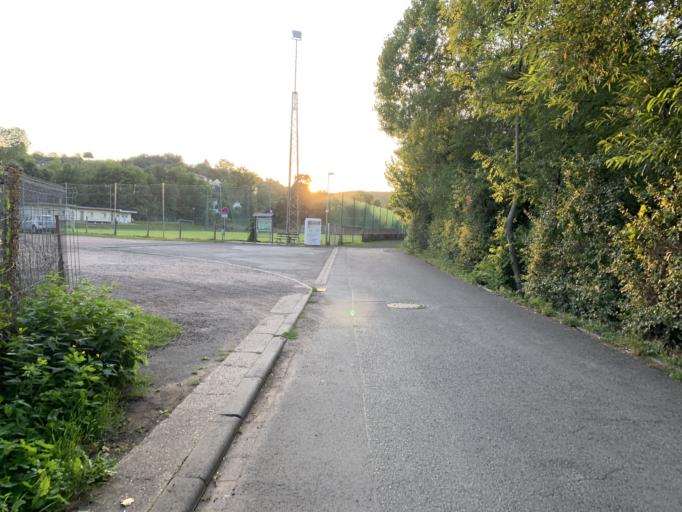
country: DE
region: Rheinland-Pfalz
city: Windesheim
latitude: 49.9081
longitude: 7.8114
